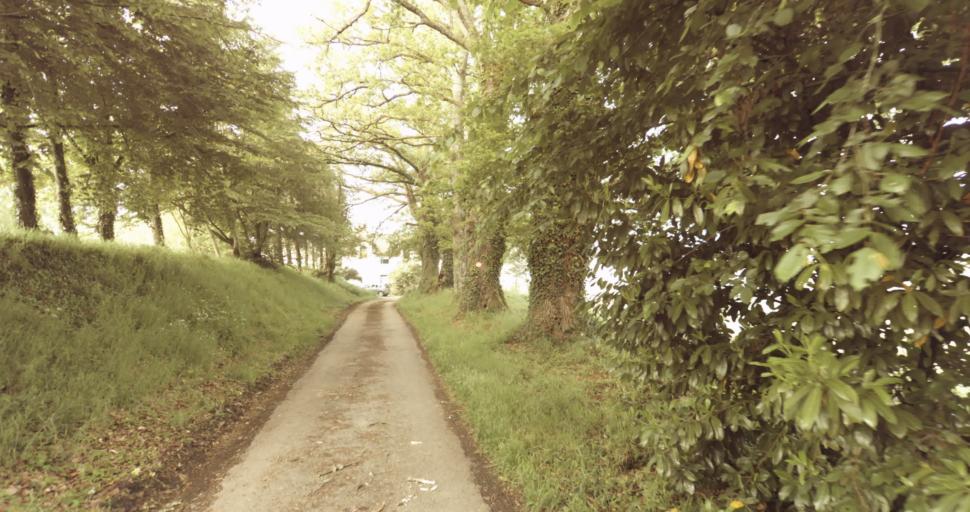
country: FR
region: Limousin
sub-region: Departement de la Haute-Vienne
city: Le Vigen
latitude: 45.7596
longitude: 1.2898
